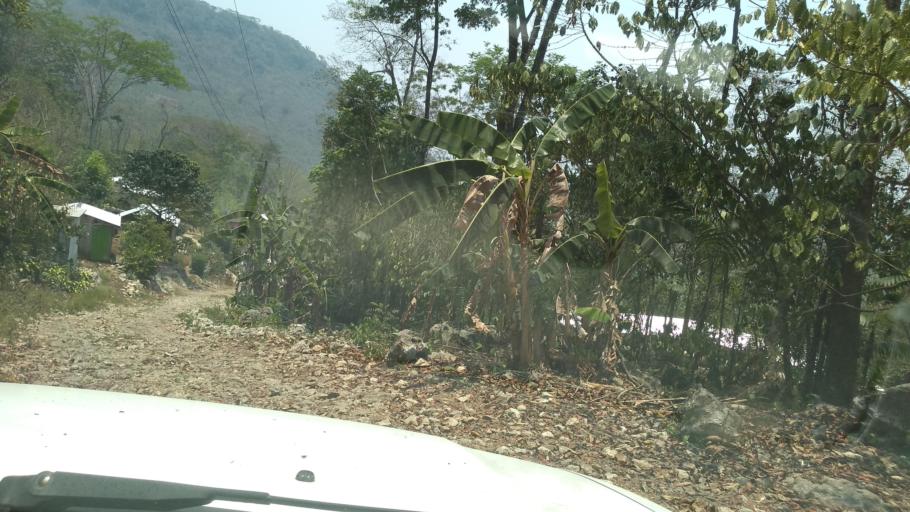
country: MX
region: Veracruz
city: Cosolapa
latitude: 18.5969
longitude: -96.7290
